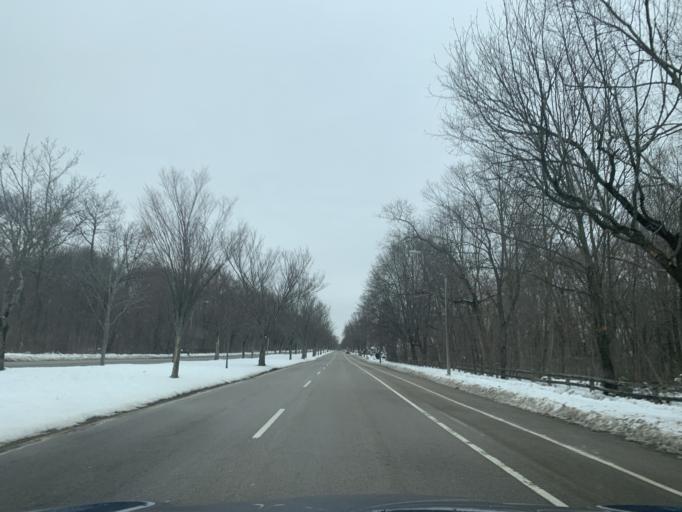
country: US
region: Massachusetts
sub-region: Norfolk County
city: Milton
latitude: 42.2515
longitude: -71.0936
